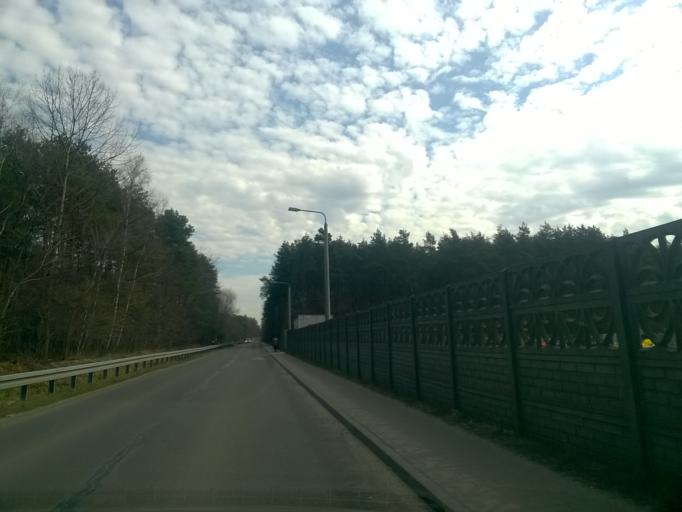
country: PL
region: Lesser Poland Voivodeship
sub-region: Powiat chrzanowski
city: Luszowice
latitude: 50.1975
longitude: 19.4395
